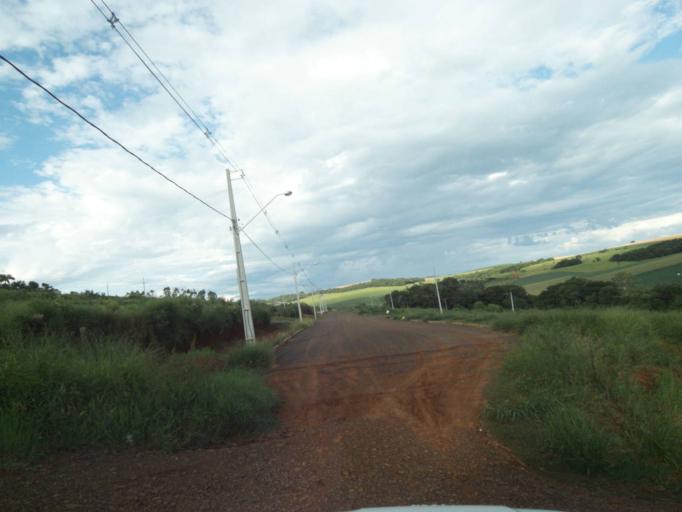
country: BR
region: Parana
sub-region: Laranjeiras Do Sul
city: Laranjeiras do Sul
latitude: -25.4909
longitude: -52.5239
